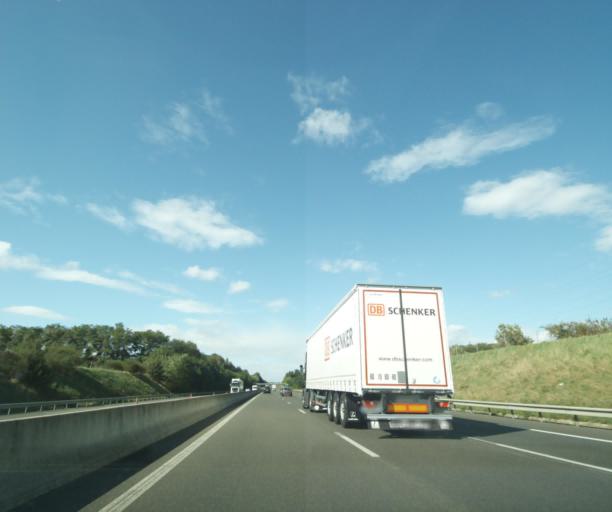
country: FR
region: Centre
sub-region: Departement du Loiret
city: Saint-Pryve-Saint-Mesmin
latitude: 47.8638
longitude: 1.8638
